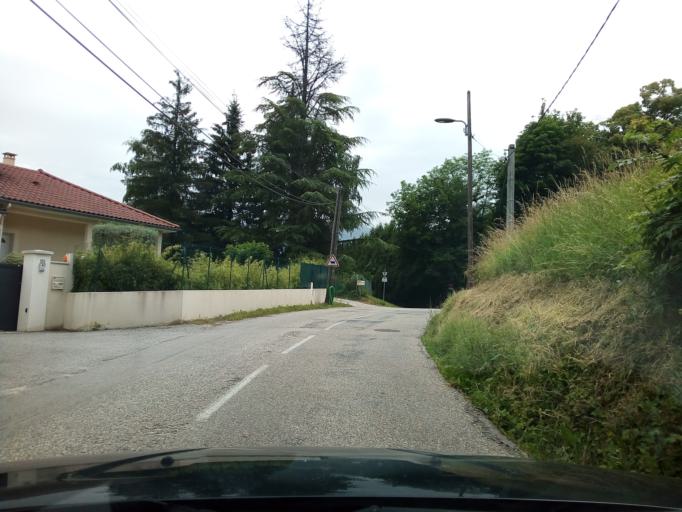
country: FR
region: Rhone-Alpes
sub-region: Departement de l'Isere
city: Gieres
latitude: 45.1737
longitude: 5.7812
